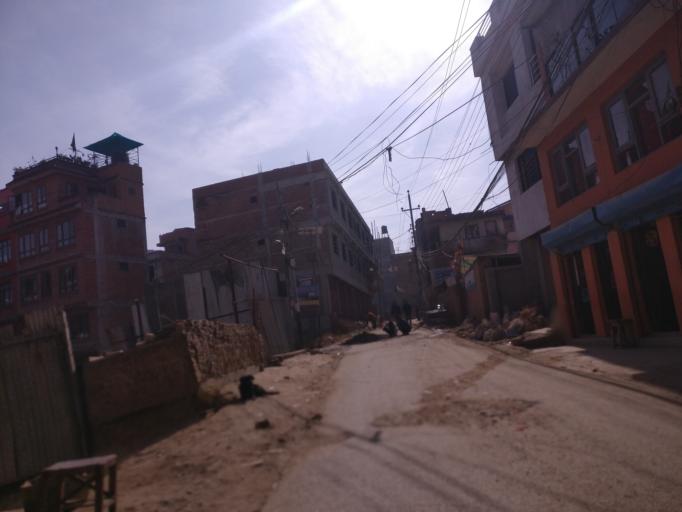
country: NP
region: Central Region
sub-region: Bagmati Zone
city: Patan
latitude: 27.6726
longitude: 85.3325
